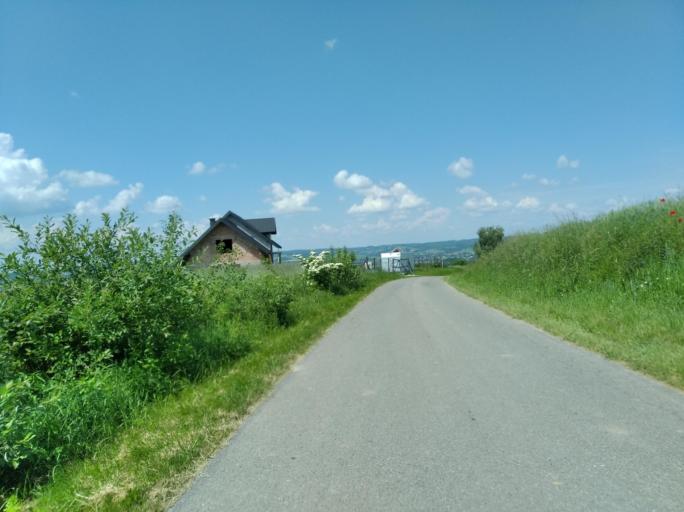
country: PL
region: Subcarpathian Voivodeship
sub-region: Powiat ropczycko-sedziszowski
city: Wielopole Skrzynskie
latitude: 49.9843
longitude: 21.6086
